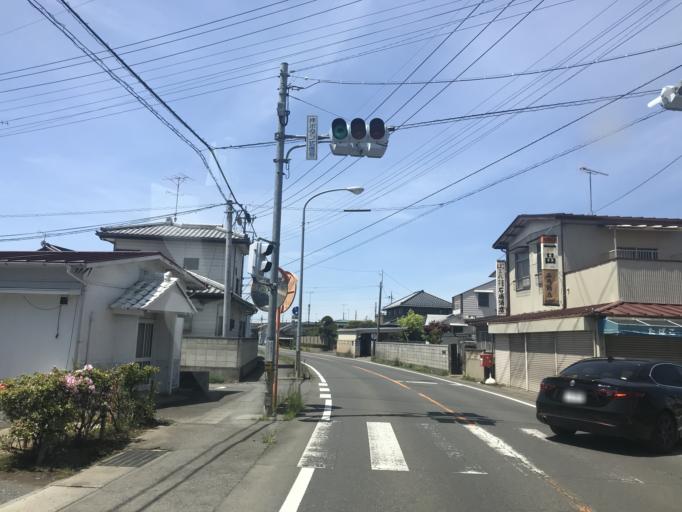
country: JP
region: Ibaraki
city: Shimodate
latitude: 36.3055
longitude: 139.9957
